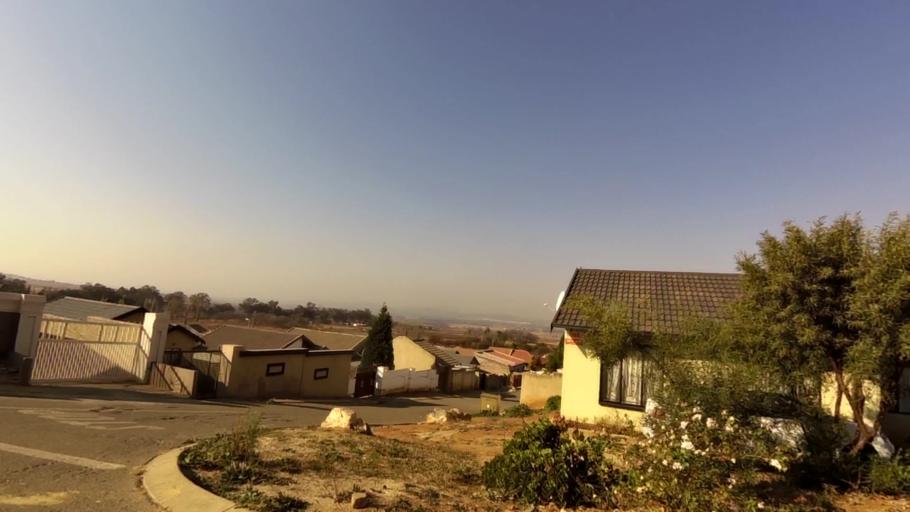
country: ZA
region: Gauteng
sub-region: City of Johannesburg Metropolitan Municipality
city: Soweto
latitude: -26.2997
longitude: 27.9486
